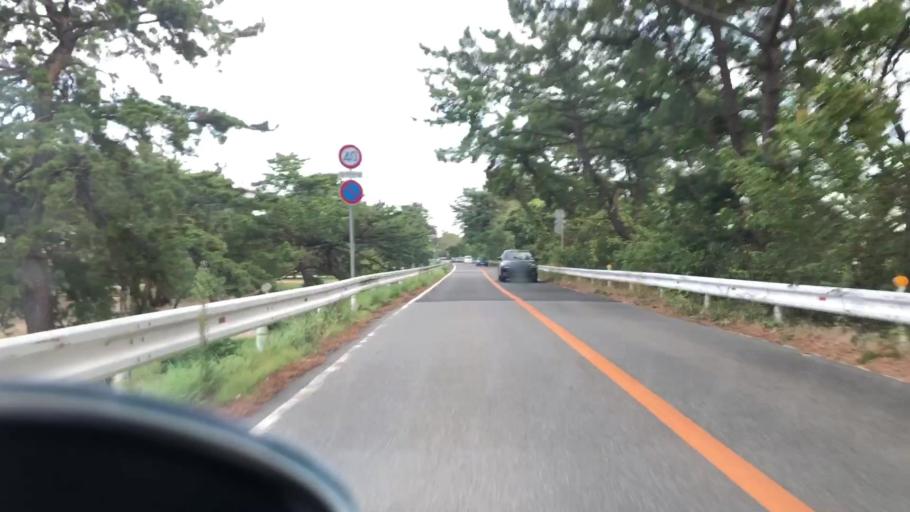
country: JP
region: Hyogo
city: Itami
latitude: 34.7572
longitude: 135.3720
